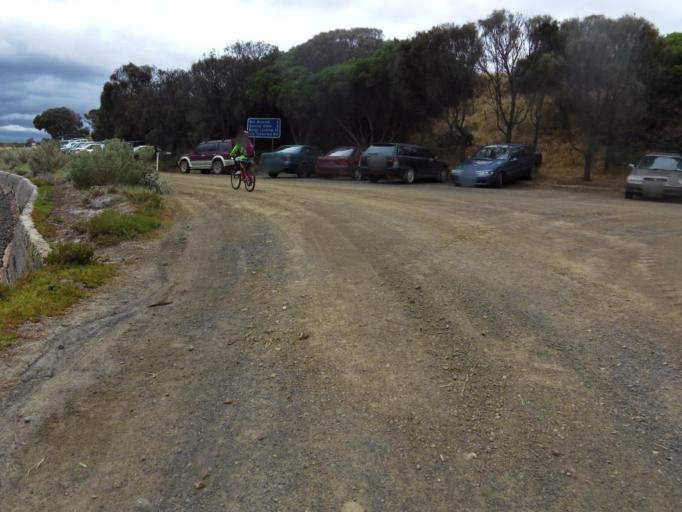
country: AU
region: Victoria
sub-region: Bass Coast
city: Cowes
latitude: -38.3828
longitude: 145.2732
